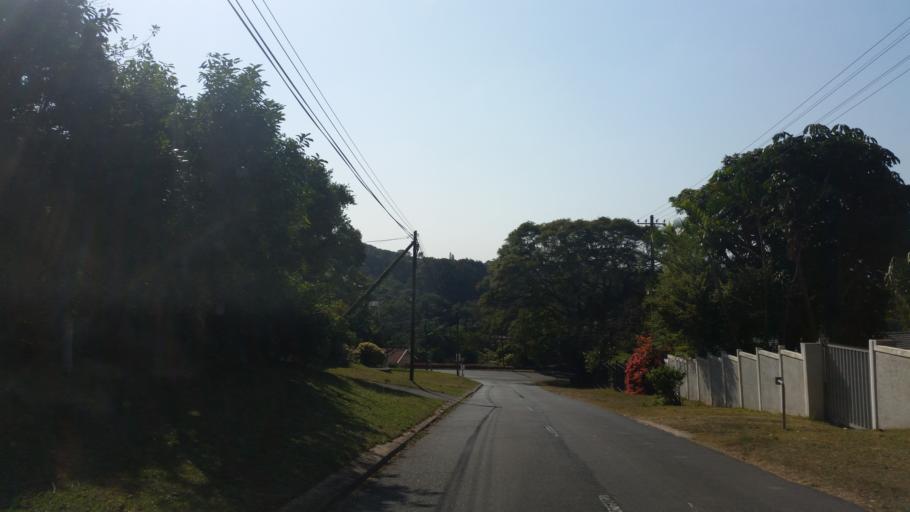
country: ZA
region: KwaZulu-Natal
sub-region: eThekwini Metropolitan Municipality
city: Berea
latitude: -29.8470
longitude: 30.9013
